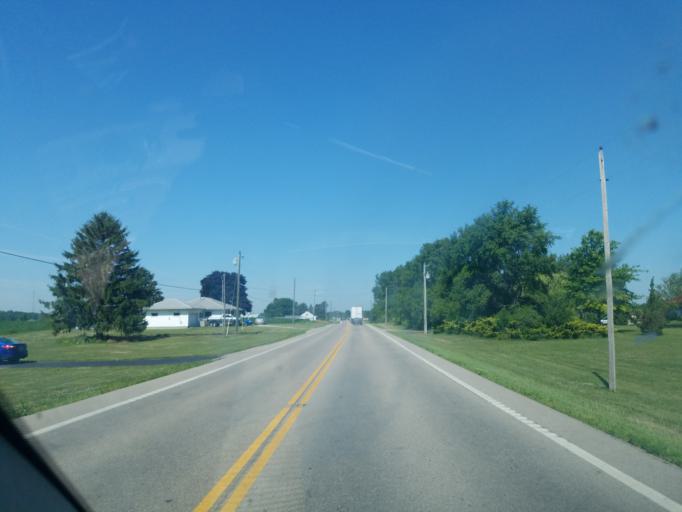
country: US
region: Ohio
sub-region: Shelby County
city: Jackson Center
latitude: 40.4394
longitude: -84.0221
